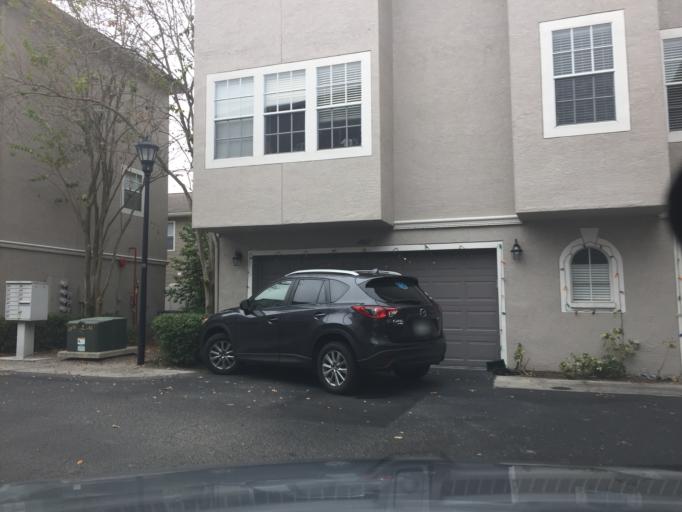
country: US
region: Florida
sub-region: Hillsborough County
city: Tampa
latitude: 27.9416
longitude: -82.4874
